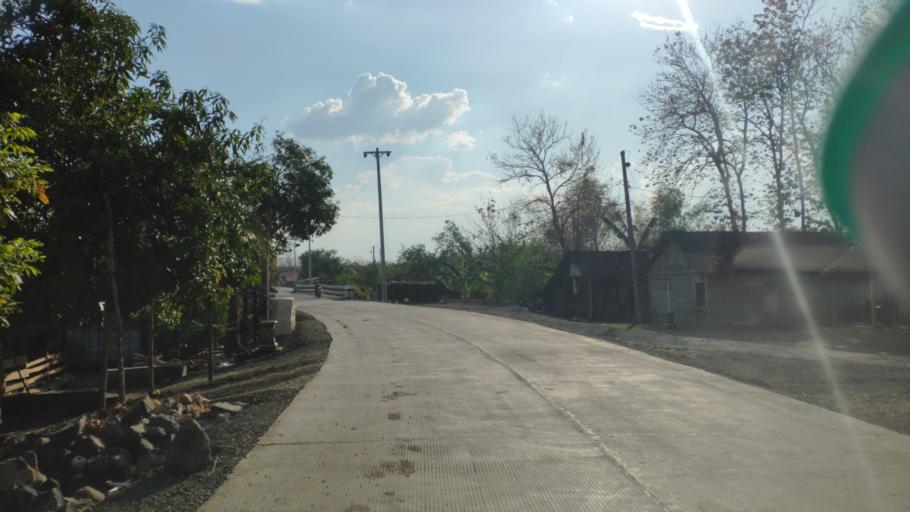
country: ID
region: Central Java
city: Ngliron
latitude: -7.1459
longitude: 111.4142
